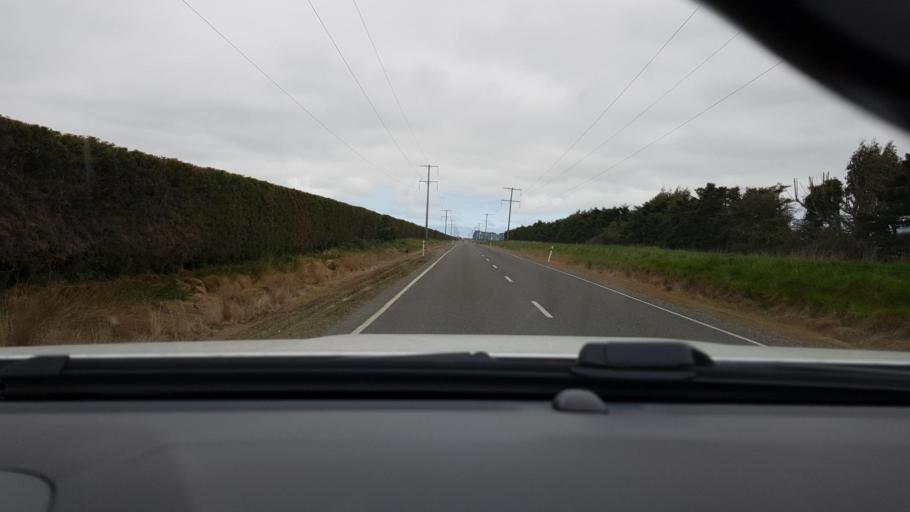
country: NZ
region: Otago
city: Oamaru
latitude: -44.9645
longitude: 171.0307
